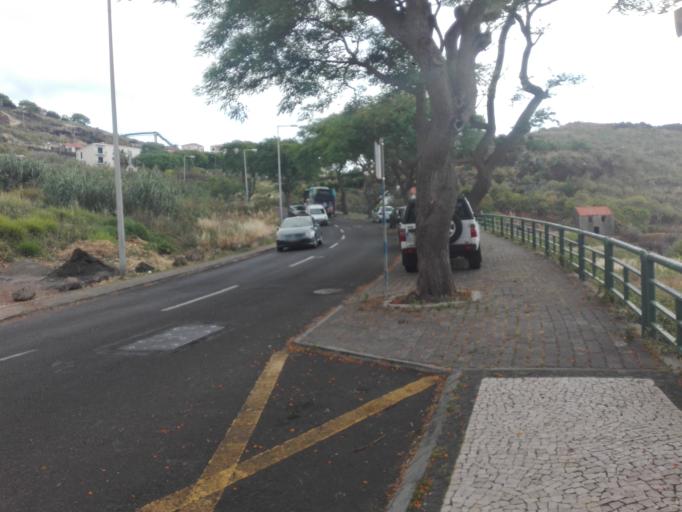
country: PT
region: Madeira
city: Canico
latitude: 32.6464
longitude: -16.8275
